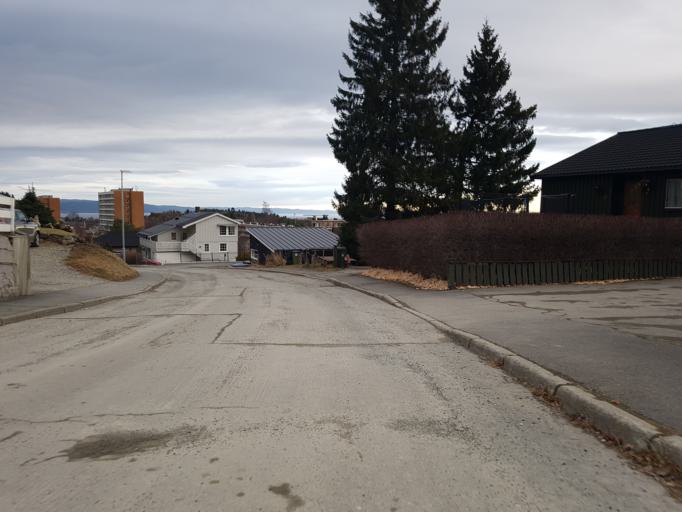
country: NO
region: Sor-Trondelag
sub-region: Trondheim
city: Trondheim
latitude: 63.4103
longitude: 10.3494
